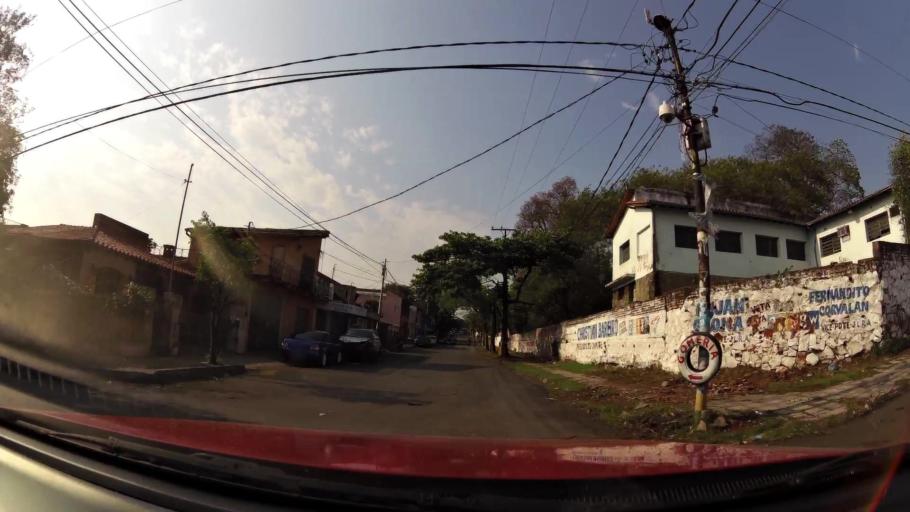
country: PY
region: Presidente Hayes
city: Nanawa
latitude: -25.2792
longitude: -57.6553
